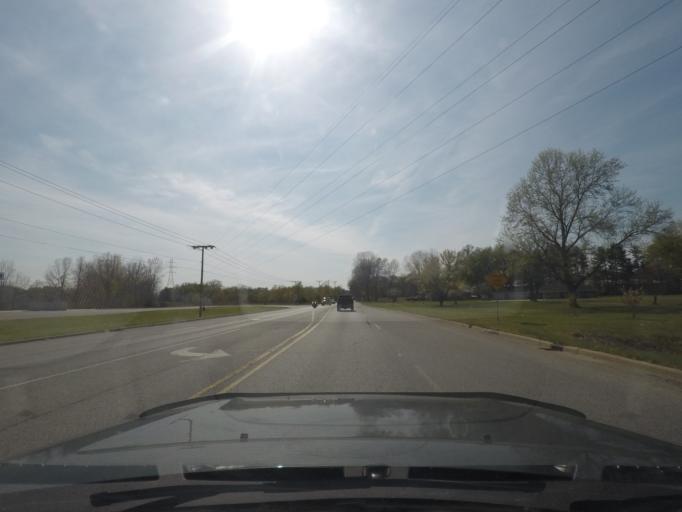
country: US
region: Indiana
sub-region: Saint Joseph County
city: Osceola
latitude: 41.7245
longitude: -86.0406
